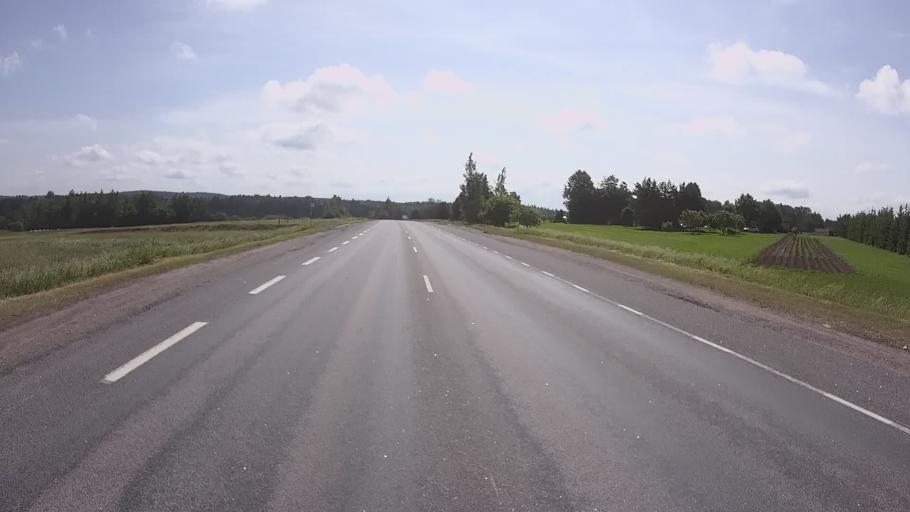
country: EE
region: Tartu
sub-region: UElenurme vald
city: Ulenurme
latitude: 58.2768
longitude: 26.7337
